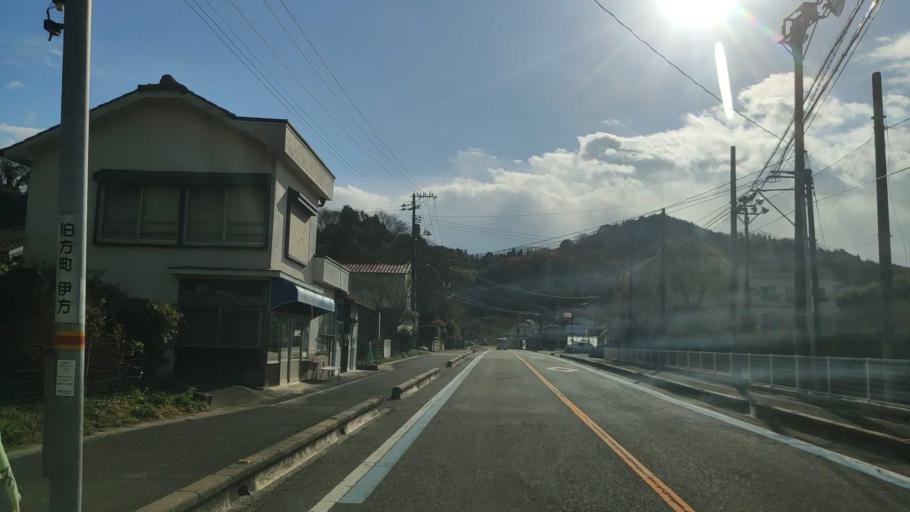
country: JP
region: Hiroshima
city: Innoshima
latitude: 34.2180
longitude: 133.0675
